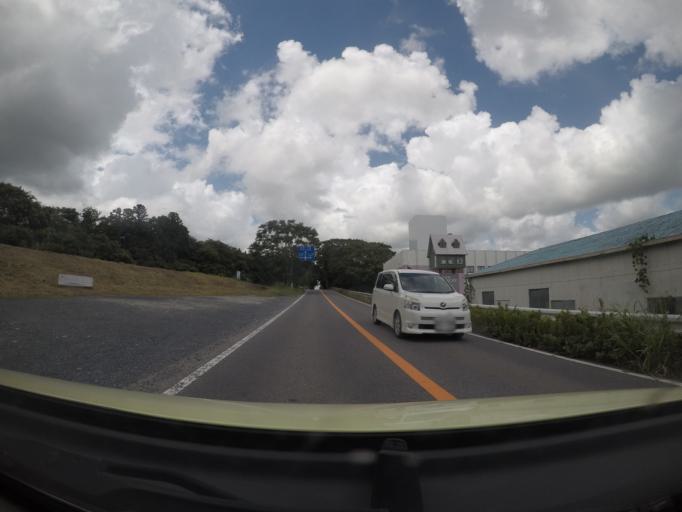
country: JP
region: Ibaraki
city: Mitsukaido
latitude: 36.0619
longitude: 139.9801
